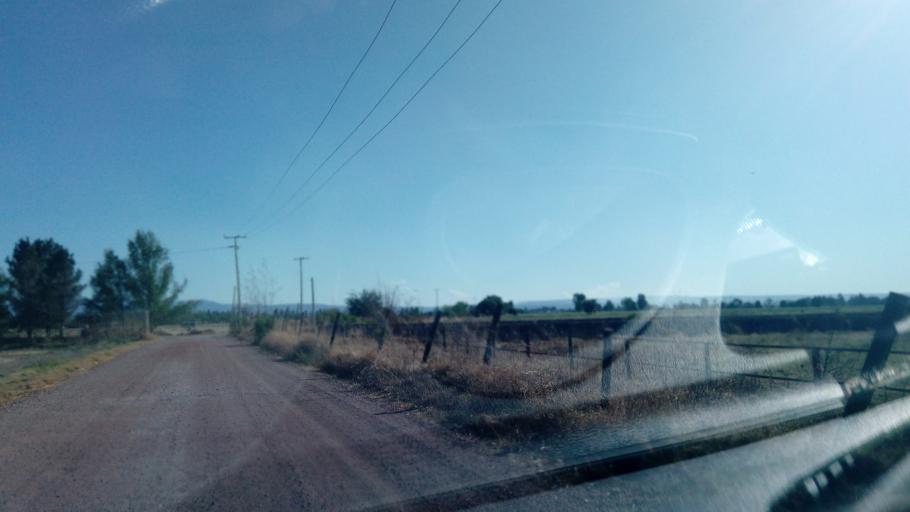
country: MX
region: Durango
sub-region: Durango
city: Jose Refugio Salcido
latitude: 24.0139
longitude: -104.5543
